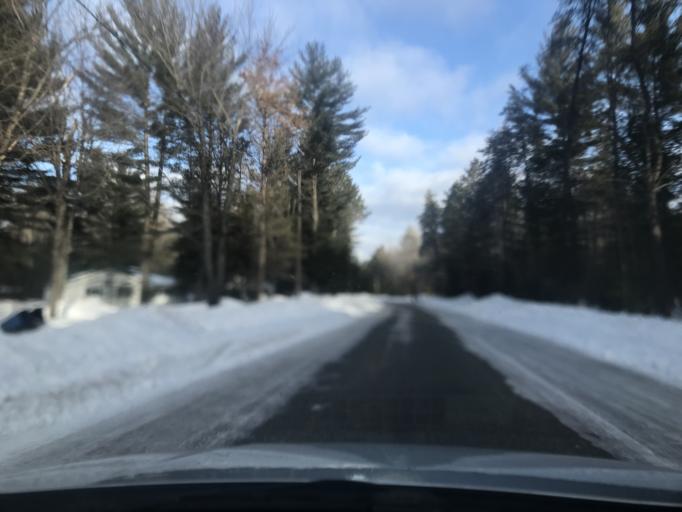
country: US
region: Wisconsin
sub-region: Marinette County
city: Niagara
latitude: 45.6342
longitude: -87.9685
